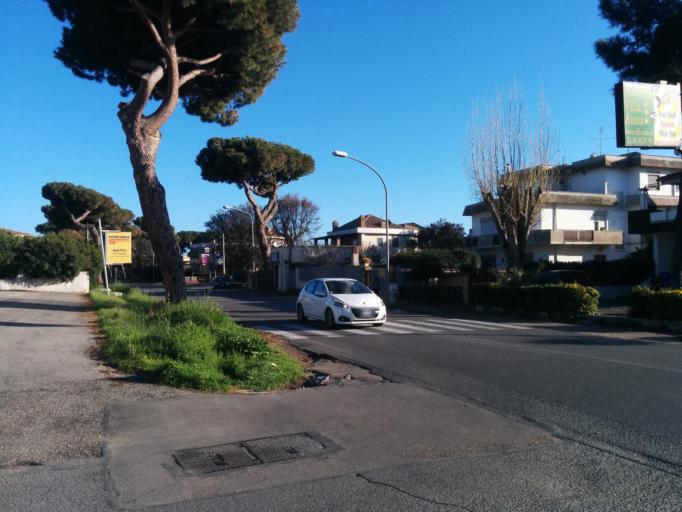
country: IT
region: Latium
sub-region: Citta metropolitana di Roma Capitale
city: Lavinio
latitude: 41.4977
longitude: 12.5904
